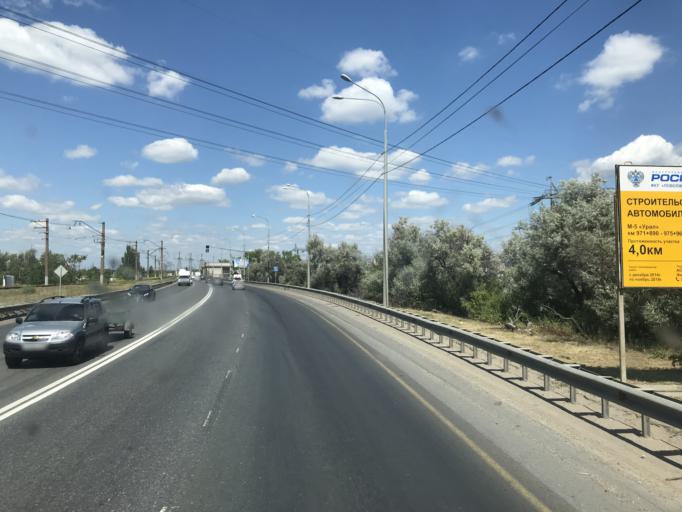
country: RU
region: Samara
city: Zhigulevsk
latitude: 53.4622
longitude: 49.5017
